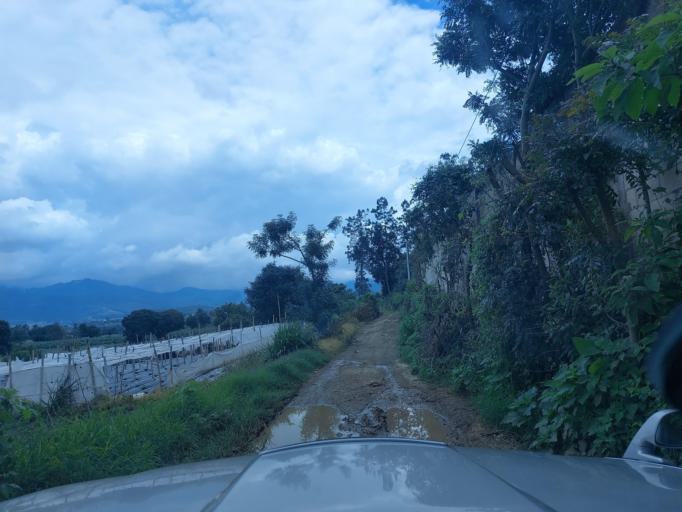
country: GT
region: Chimaltenango
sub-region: Municipio de Chimaltenango
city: Chimaltenango
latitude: 14.6479
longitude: -90.8274
